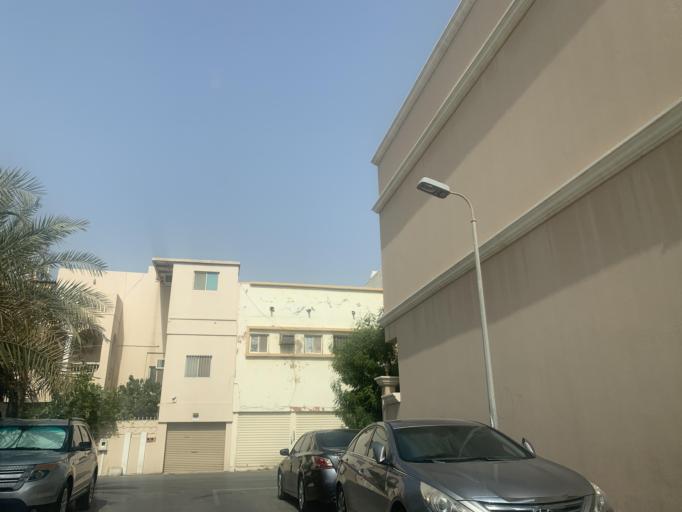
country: BH
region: Manama
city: Jidd Hafs
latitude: 26.2116
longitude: 50.4668
